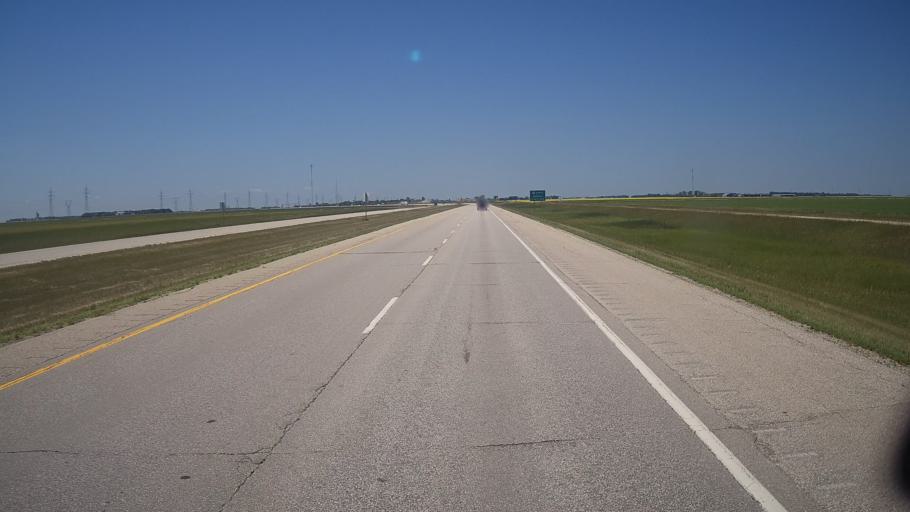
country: CA
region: Manitoba
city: Stonewall
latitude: 49.9900
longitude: -97.2911
